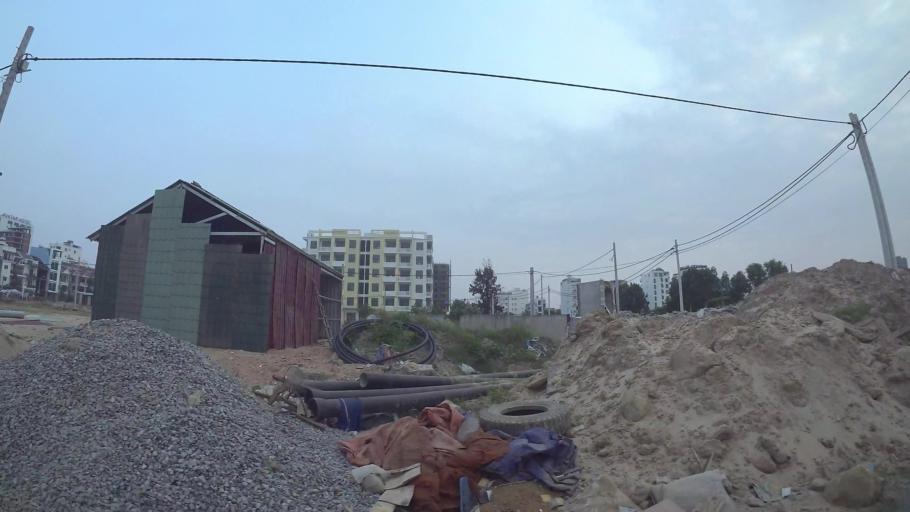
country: VN
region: Da Nang
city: Son Tra
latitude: 16.0508
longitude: 108.2429
